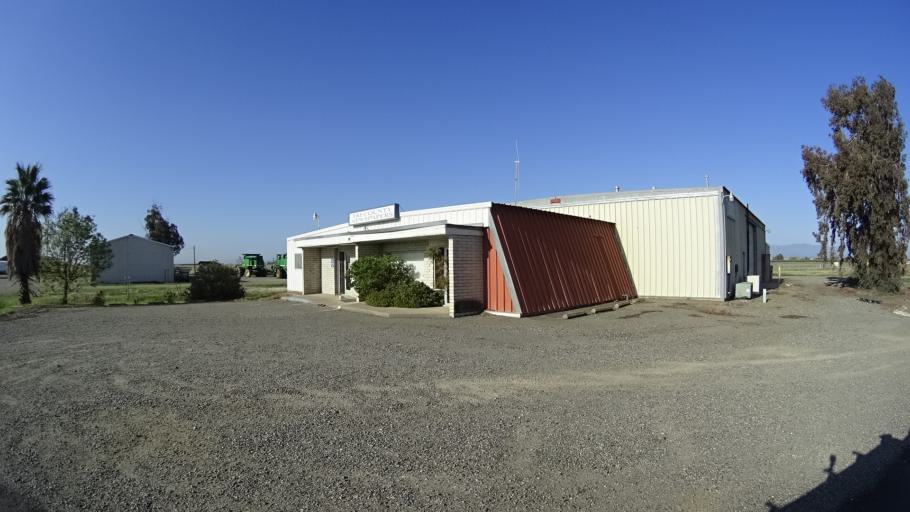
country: US
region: California
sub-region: Glenn County
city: Willows
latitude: 39.5207
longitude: -122.2152
